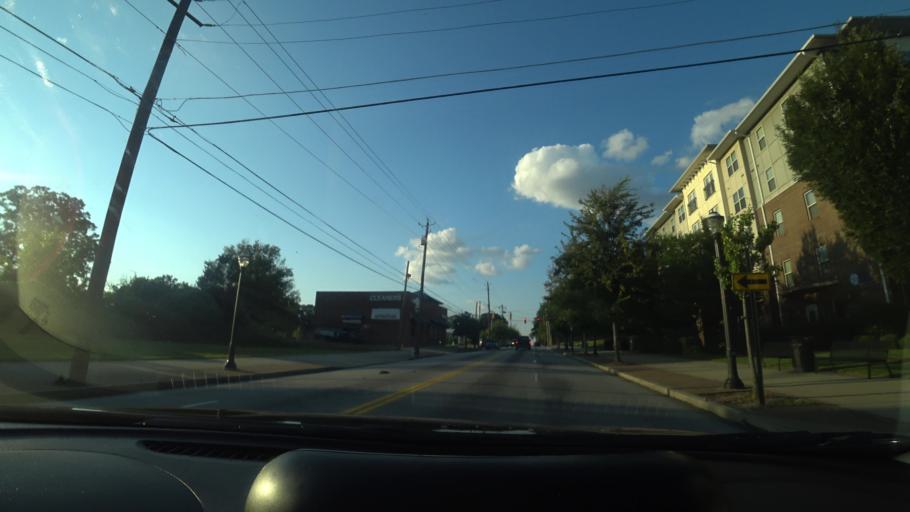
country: US
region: Georgia
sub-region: Fulton County
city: Atlanta
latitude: 33.7134
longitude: -84.3934
